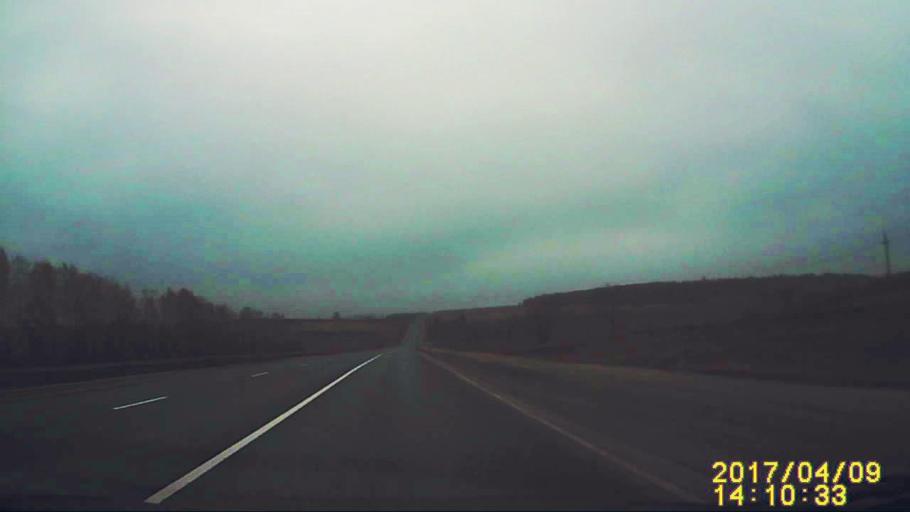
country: RU
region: Ulyanovsk
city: Krasnyy Gulyay
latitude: 54.0396
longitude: 48.2136
